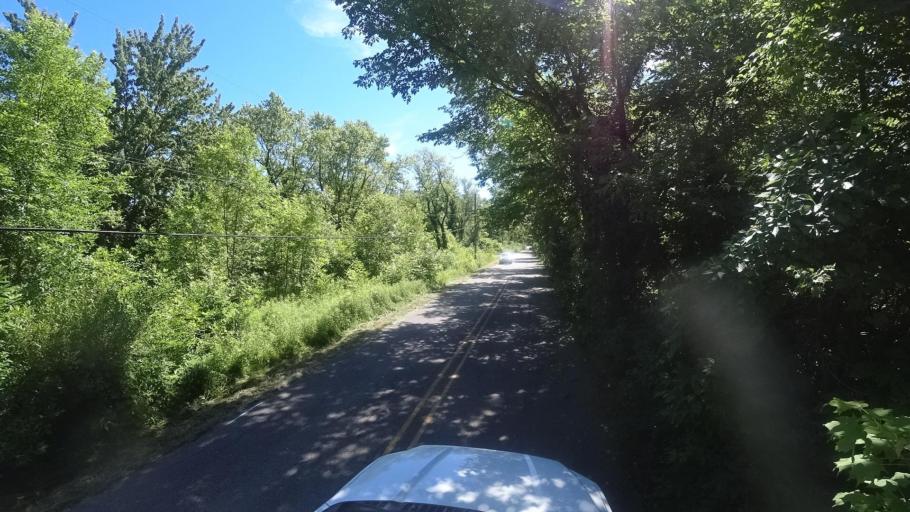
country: US
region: Indiana
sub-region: Porter County
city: Porter
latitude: 41.6297
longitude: -87.0950
